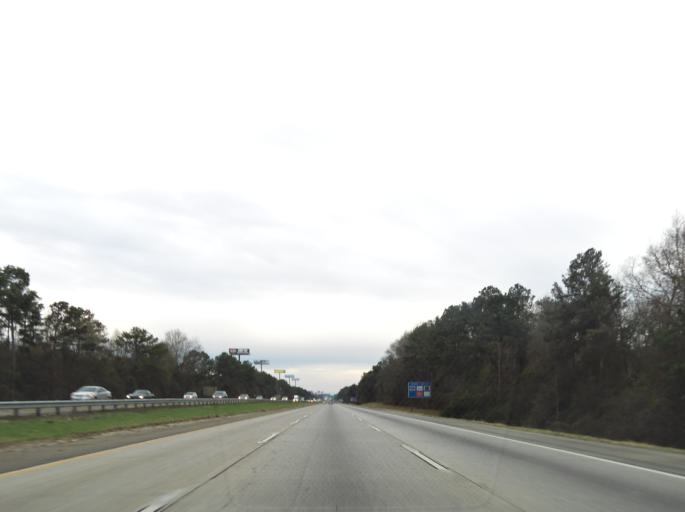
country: US
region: Georgia
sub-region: Peach County
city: Byron
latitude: 32.6392
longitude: -83.7440
